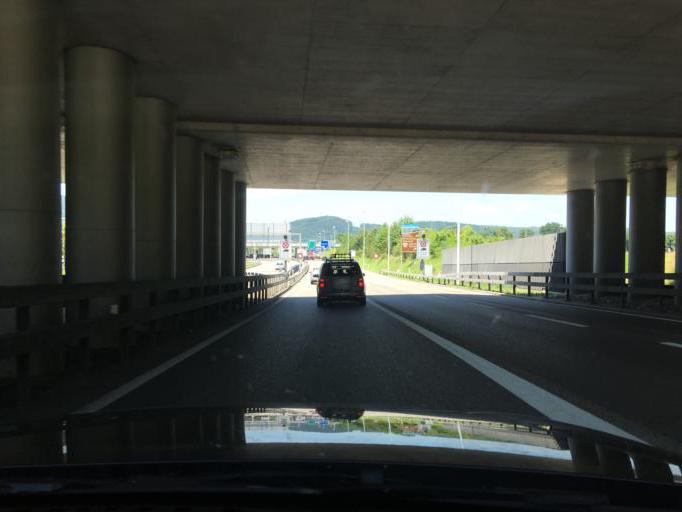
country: CH
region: Basel-Landschaft
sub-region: Bezirk Liestal
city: Arisdorf
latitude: 47.5441
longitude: 7.7597
